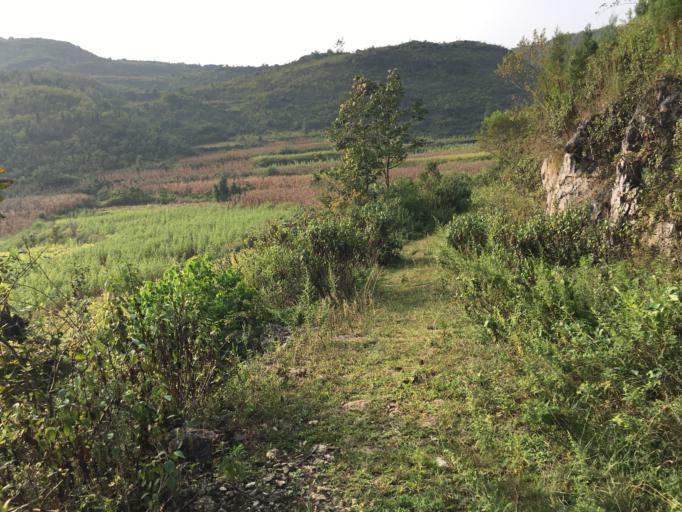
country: CN
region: Guangxi Zhuangzu Zizhiqu
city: Xinzhou
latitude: 25.4406
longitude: 105.6364
